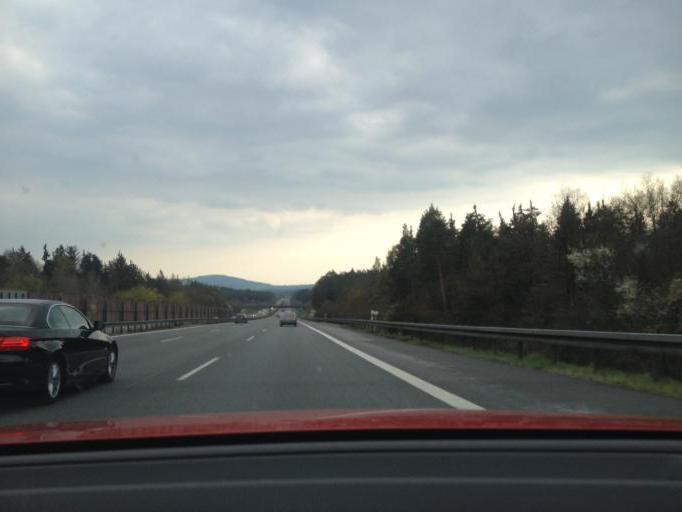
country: DE
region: Bavaria
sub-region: Regierungsbezirk Mittelfranken
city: Schnaittach
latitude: 49.5564
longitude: 11.3239
